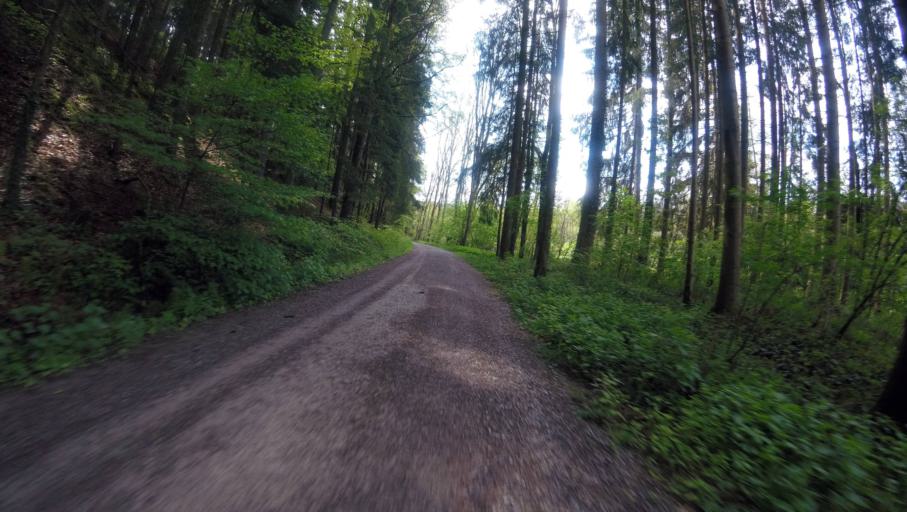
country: DE
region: Baden-Wuerttemberg
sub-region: Regierungsbezirk Stuttgart
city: Spraitbach
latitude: 48.8610
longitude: 9.7576
